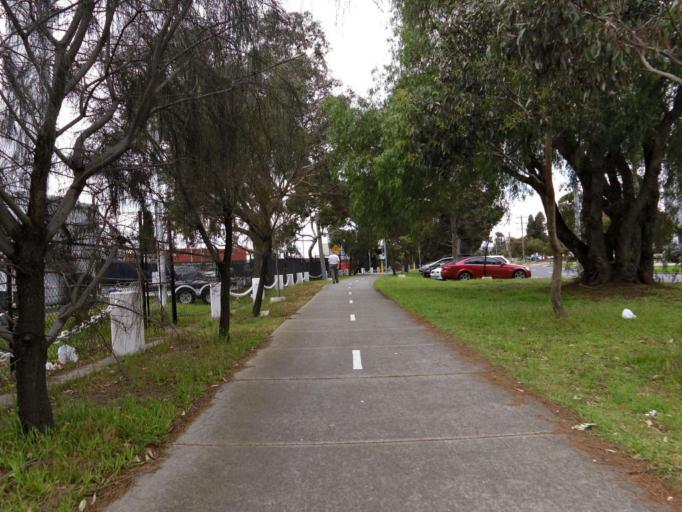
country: AU
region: Victoria
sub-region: Maribyrnong
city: Yarraville
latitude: -37.8235
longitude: 144.9083
